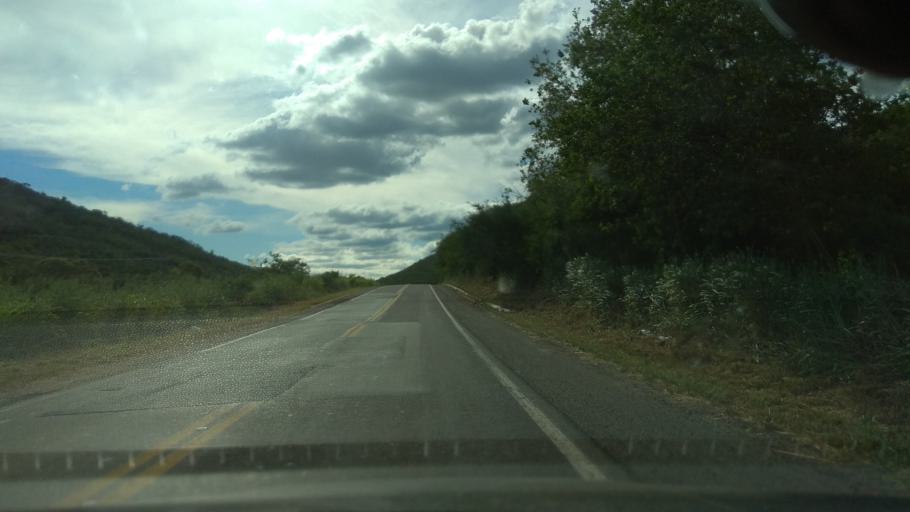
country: BR
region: Bahia
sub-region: Jequie
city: Jequie
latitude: -13.8966
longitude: -40.0202
